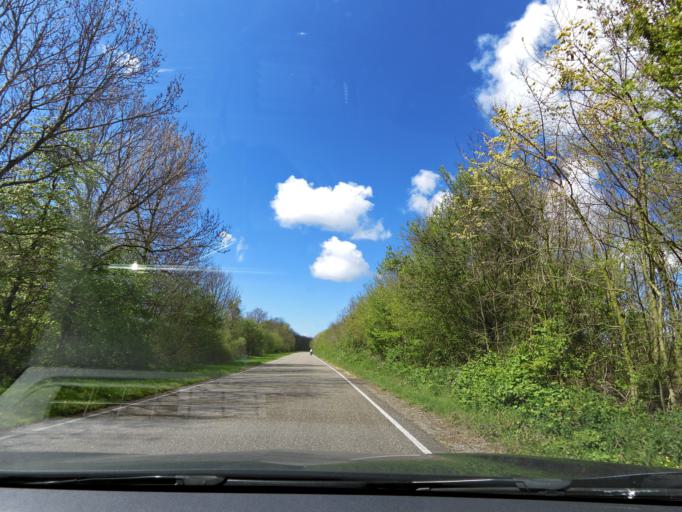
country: NL
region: South Holland
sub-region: Gemeente Brielle
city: Brielle
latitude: 51.9271
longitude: 4.1581
